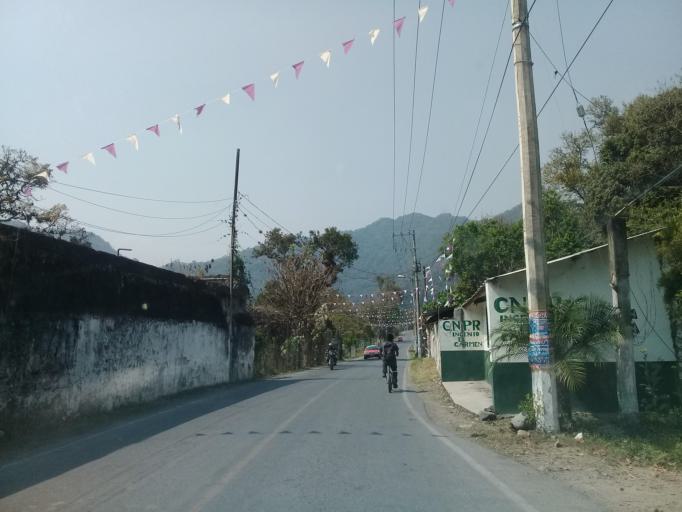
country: MX
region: Veracruz
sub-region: Ixtaczoquitlan
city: Campo Chico
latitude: 18.8301
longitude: -97.0227
